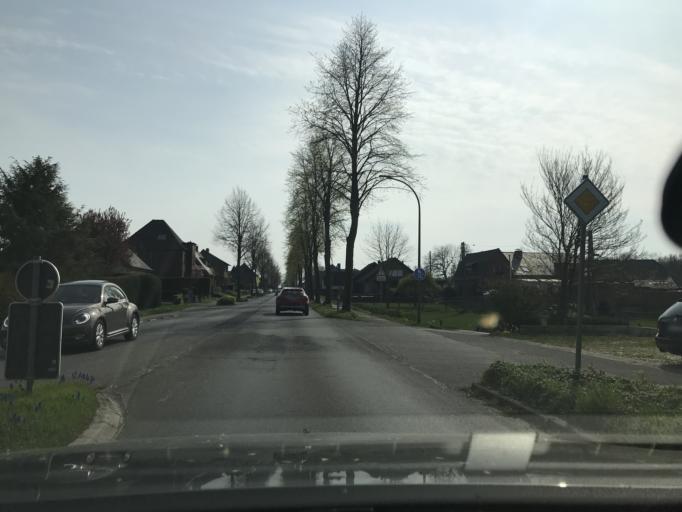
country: DE
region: North Rhine-Westphalia
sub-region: Regierungsbezirk Dusseldorf
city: Goch
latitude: 51.7067
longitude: 6.1569
